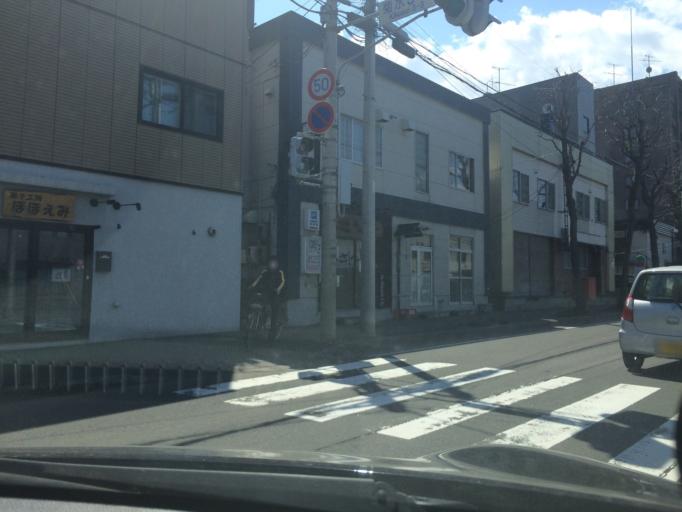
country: JP
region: Hokkaido
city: Sapporo
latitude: 43.0571
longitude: 141.3753
